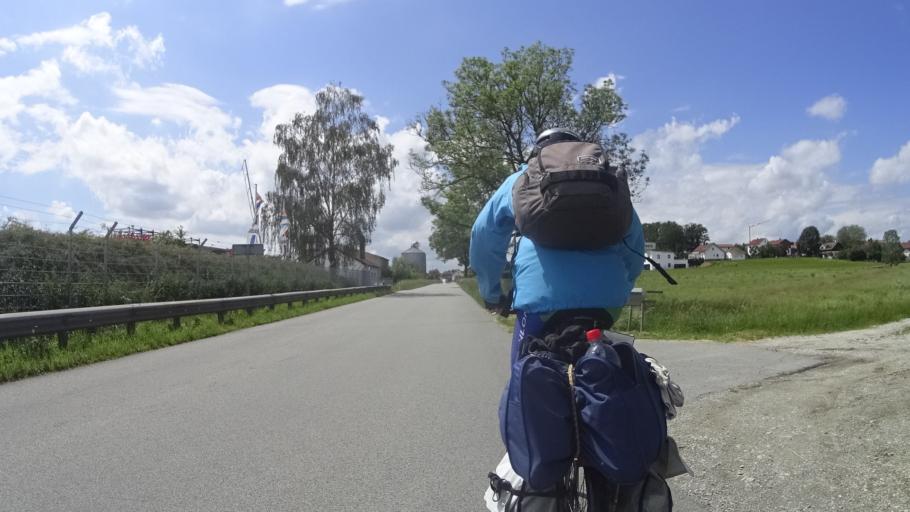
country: DE
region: Bavaria
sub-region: Lower Bavaria
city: Unterdietfurt
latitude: 48.3944
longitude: 12.6755
